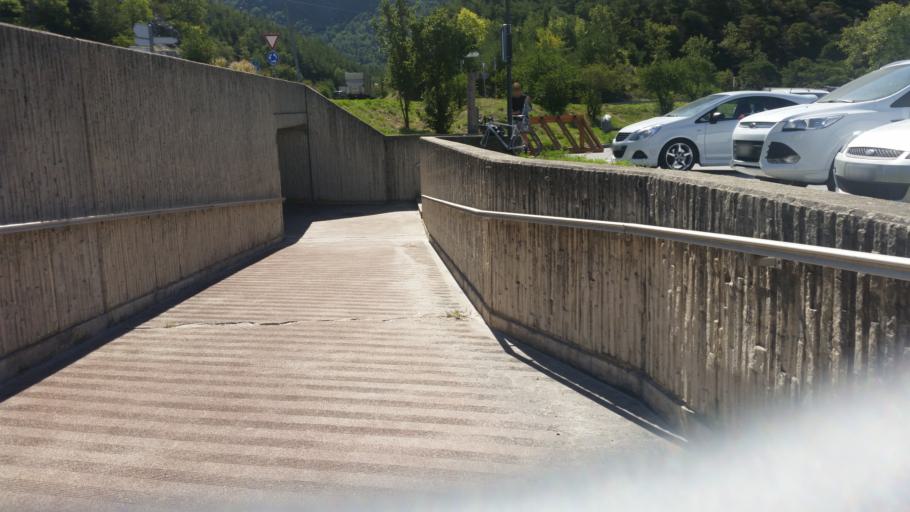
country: CH
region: Valais
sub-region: Sierre District
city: Chippis
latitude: 46.2936
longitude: 7.5569
